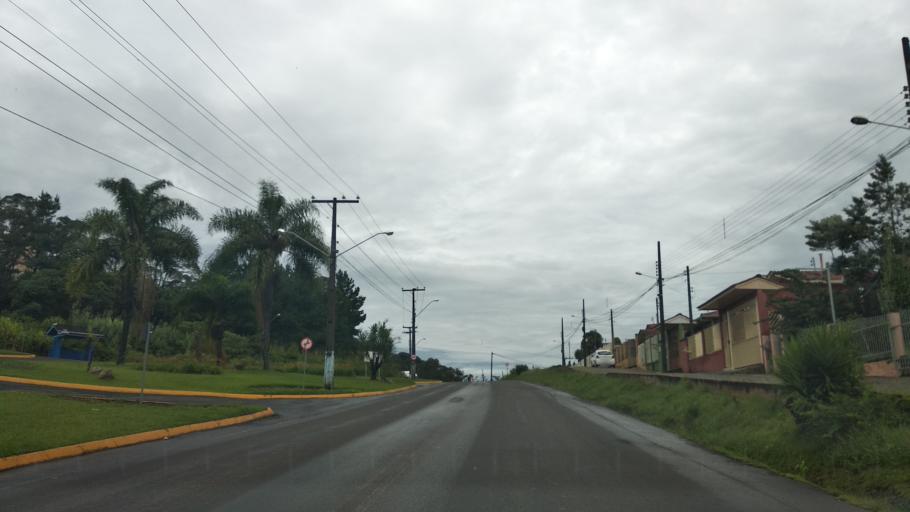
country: BR
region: Santa Catarina
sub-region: Videira
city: Videira
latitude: -26.9931
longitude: -51.1814
